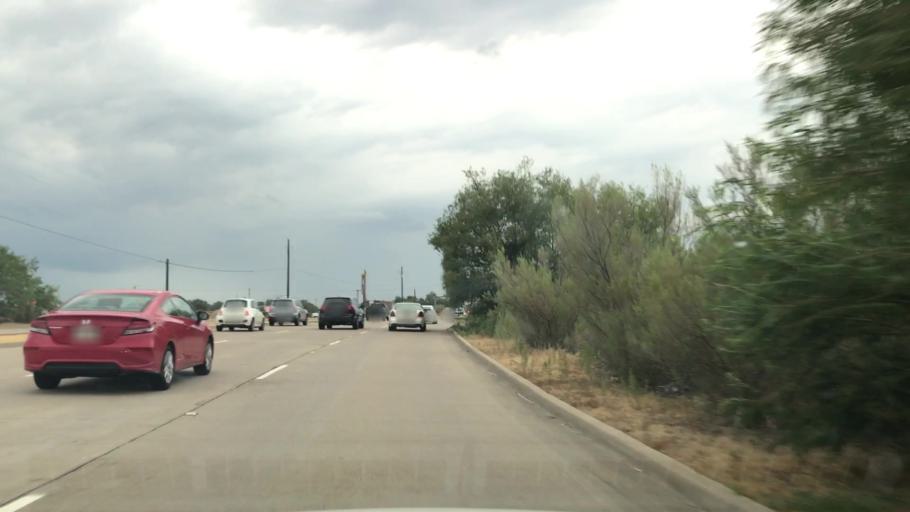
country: US
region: Texas
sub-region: Dallas County
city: Carrollton
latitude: 32.9572
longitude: -96.9240
